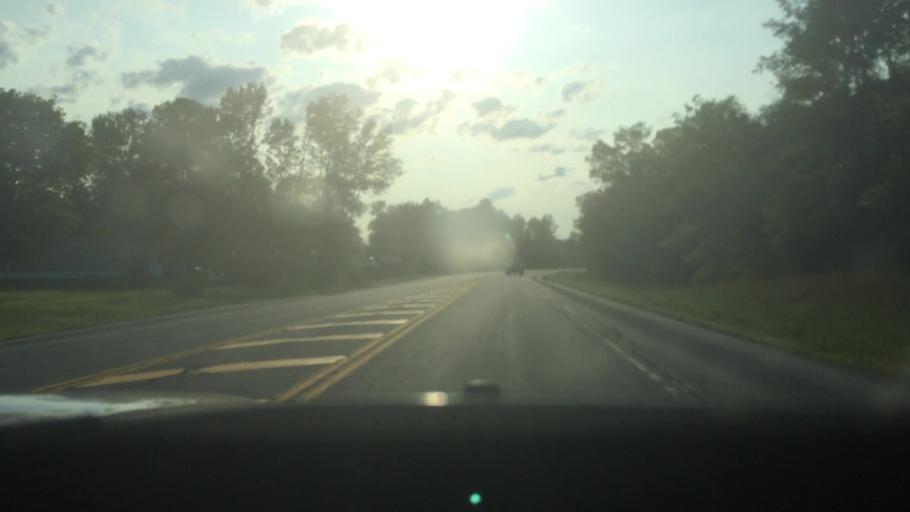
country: US
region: New York
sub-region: St. Lawrence County
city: Ogdensburg
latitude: 44.6722
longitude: -75.4272
